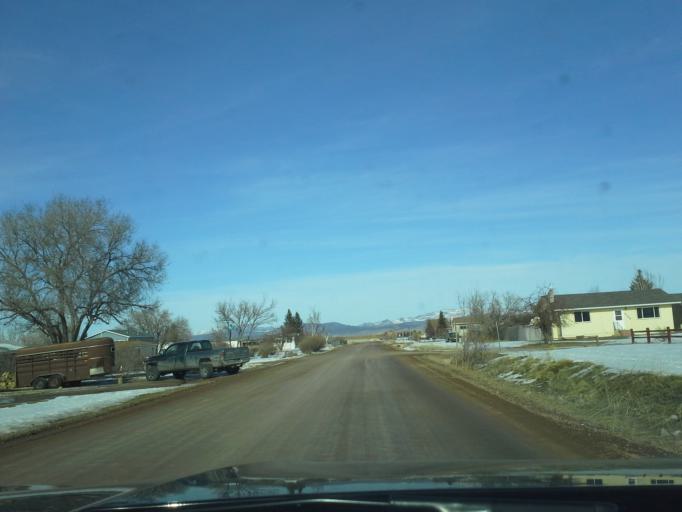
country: US
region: Montana
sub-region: Lewis and Clark County
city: East Helena
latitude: 46.5927
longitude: -111.8991
